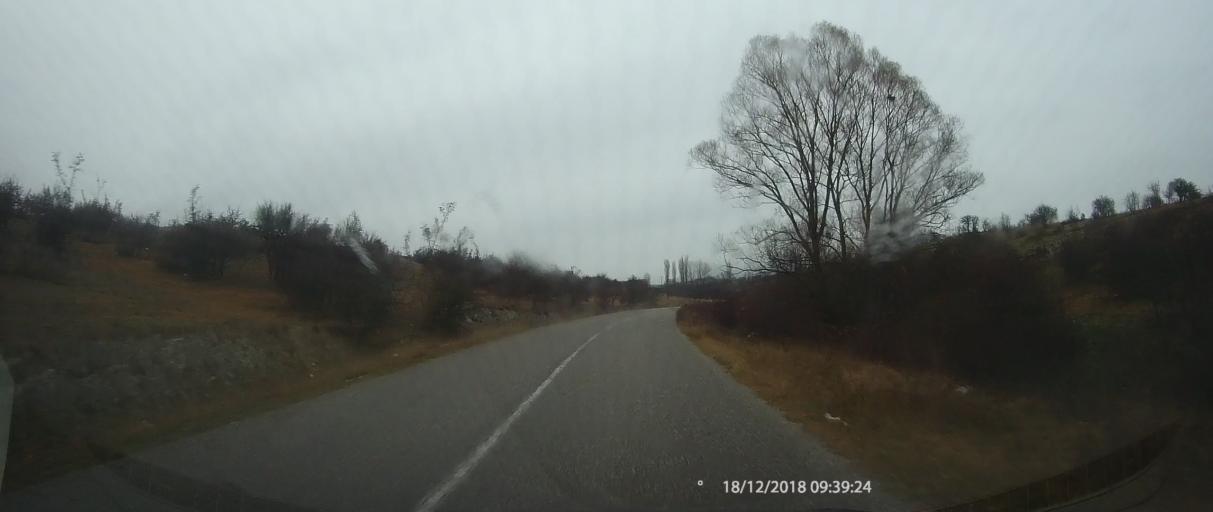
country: GR
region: Thessaly
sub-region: Nomos Larisis
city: Elassona
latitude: 39.9988
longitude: 22.2156
